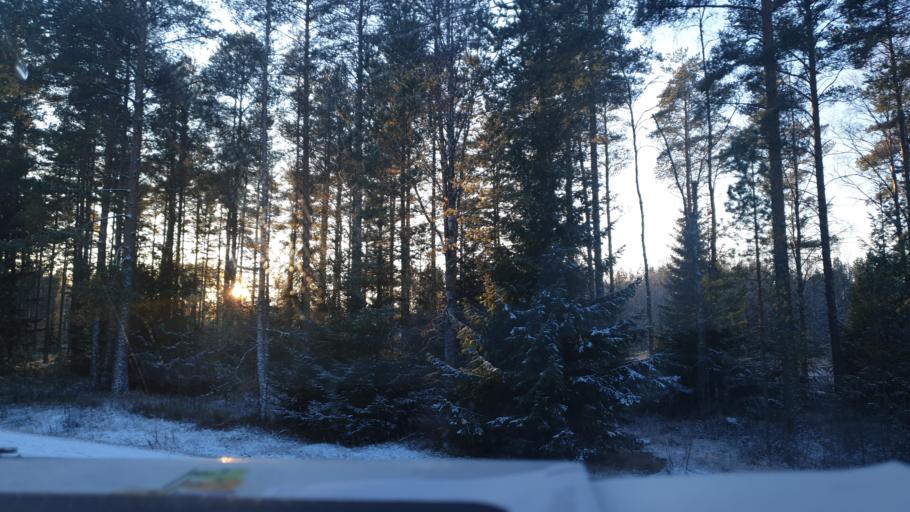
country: FI
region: Central Ostrobothnia
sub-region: Kokkola
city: Kokkola
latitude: 63.8216
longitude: 23.0689
